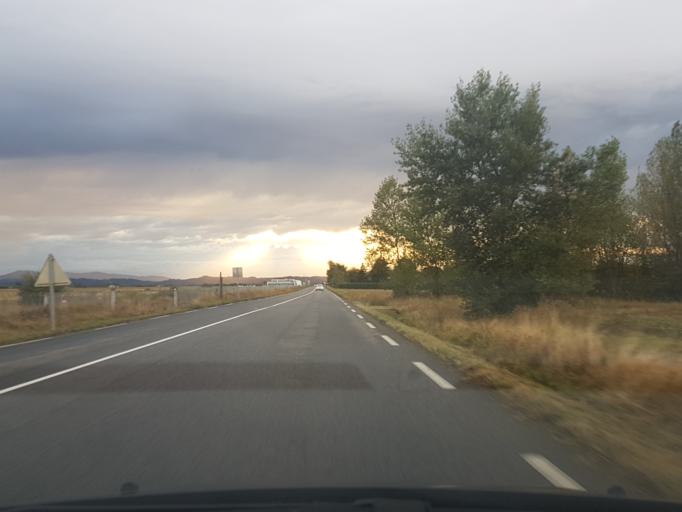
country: FR
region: Midi-Pyrenees
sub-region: Departement de l'Ariege
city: La Tour-du-Crieu
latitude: 43.0924
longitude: 1.7069
